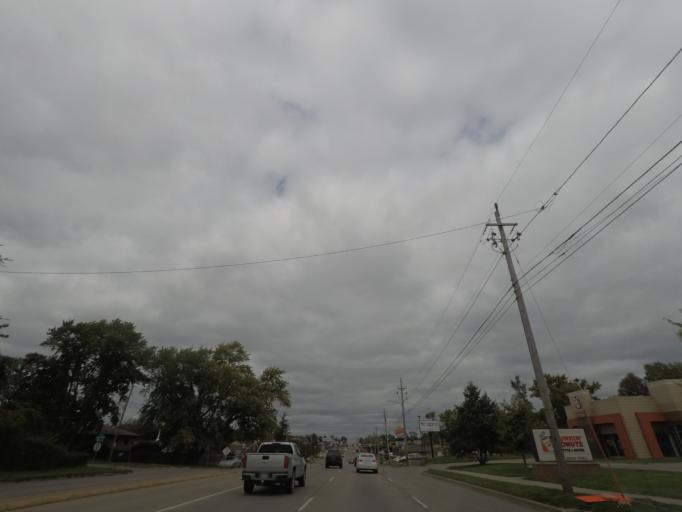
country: US
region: Iowa
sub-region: Polk County
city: Des Moines
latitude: 41.5509
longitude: -93.5967
